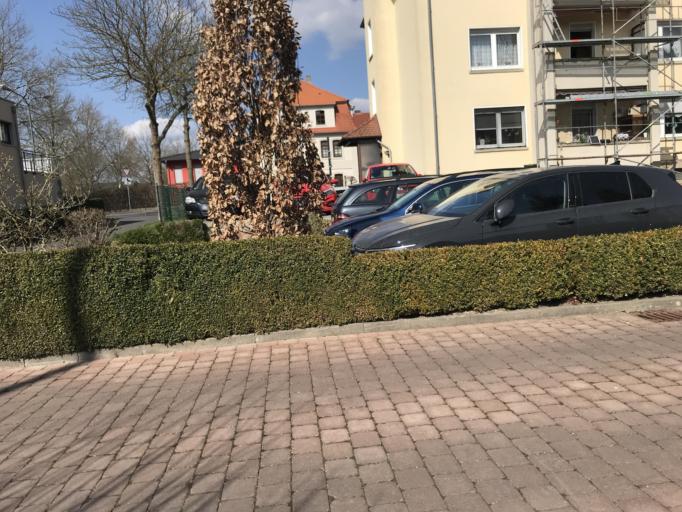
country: DE
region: Hesse
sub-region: Regierungsbezirk Kassel
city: Fulda
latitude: 50.5547
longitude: 9.6674
